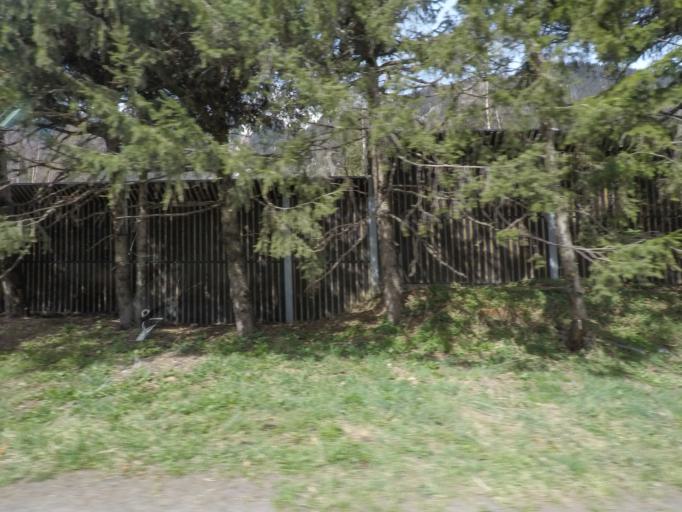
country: FR
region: Rhone-Alpes
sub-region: Departement de la Haute-Savoie
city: Chamonix-Mont-Blanc
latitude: 45.9468
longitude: 6.8943
